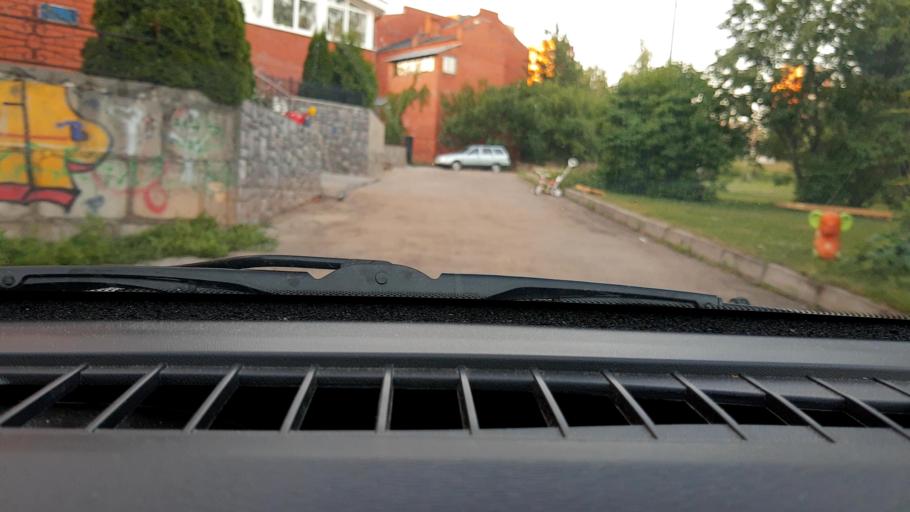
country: RU
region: Nizjnij Novgorod
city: Afonino
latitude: 56.2880
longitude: 44.0617
